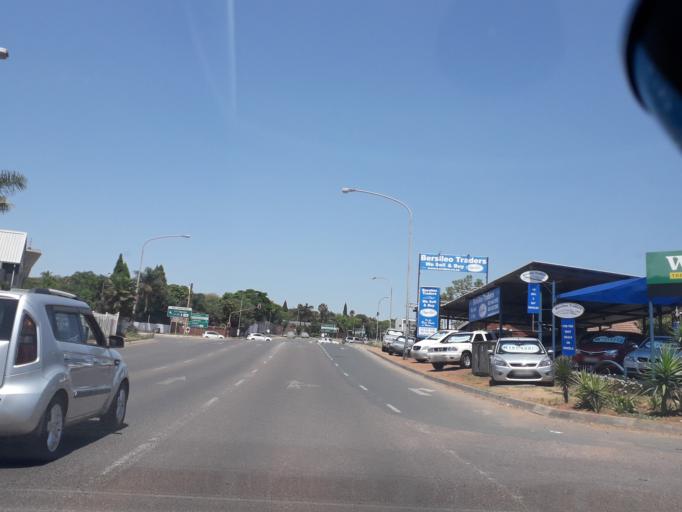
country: ZA
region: Gauteng
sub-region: City of Tshwane Metropolitan Municipality
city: Centurion
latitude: -25.8625
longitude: 28.1875
